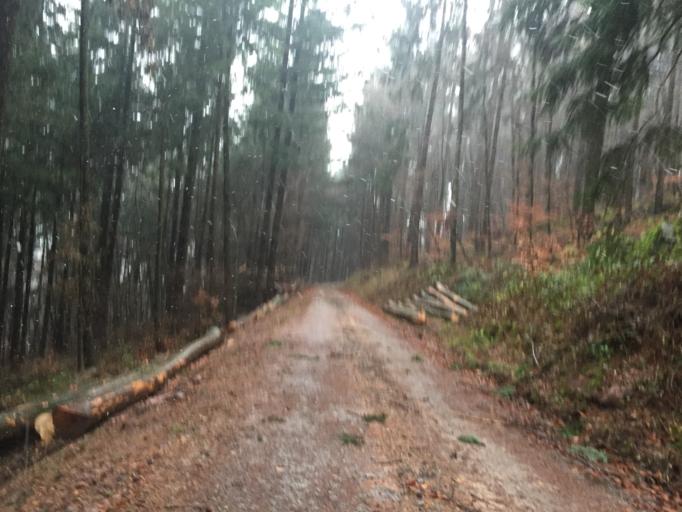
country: DE
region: Baden-Wuerttemberg
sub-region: Karlsruhe Region
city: Eberbach
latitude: 49.4606
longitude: 9.0190
